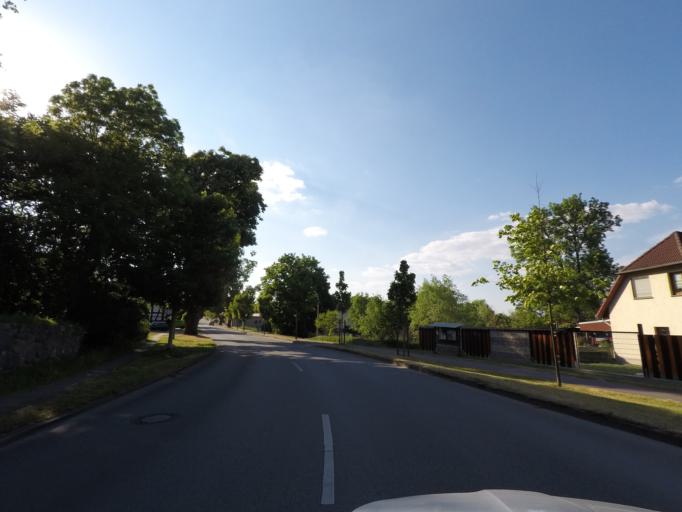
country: DE
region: Brandenburg
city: Eberswalde
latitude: 52.8239
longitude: 13.8674
